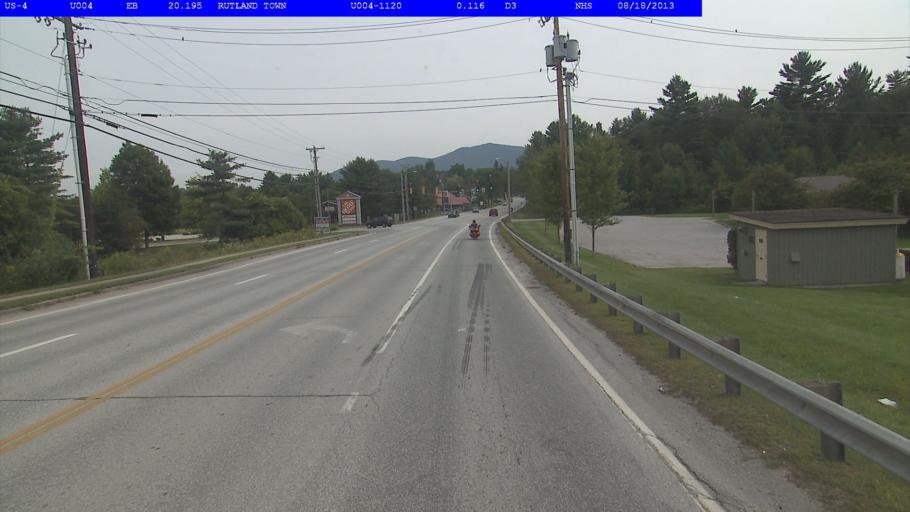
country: US
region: Vermont
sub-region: Rutland County
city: Rutland
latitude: 43.6231
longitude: -72.9525
